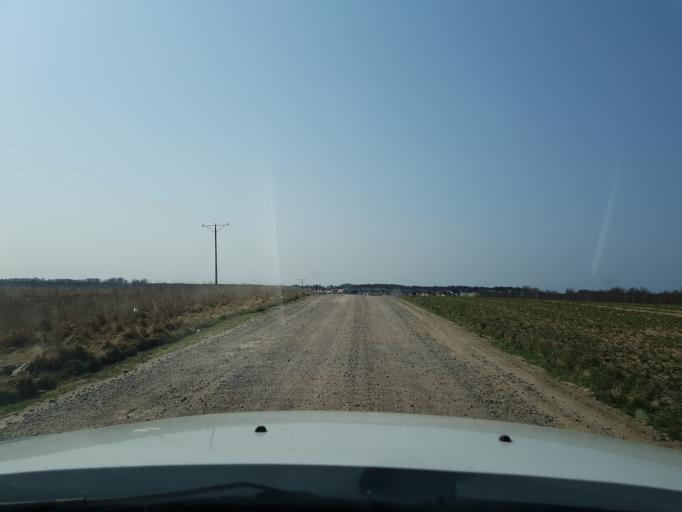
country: PL
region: West Pomeranian Voivodeship
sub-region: Powiat slawienski
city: Darlowo
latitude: 54.4430
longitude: 16.4104
